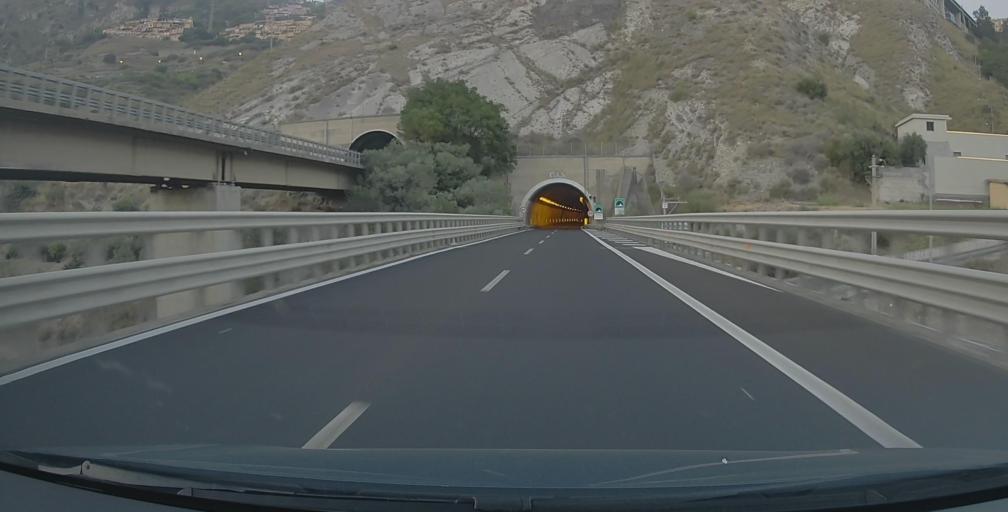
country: IT
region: Sicily
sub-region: Messina
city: Castelmola
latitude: 37.8501
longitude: 15.2760
